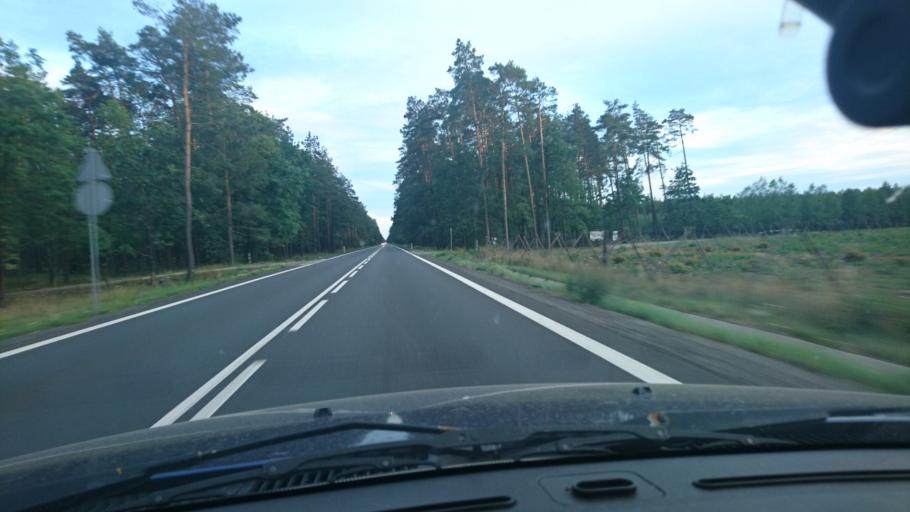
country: PL
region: Silesian Voivodeship
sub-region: Powiat tarnogorski
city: Tworog
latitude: 50.5824
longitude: 18.7074
